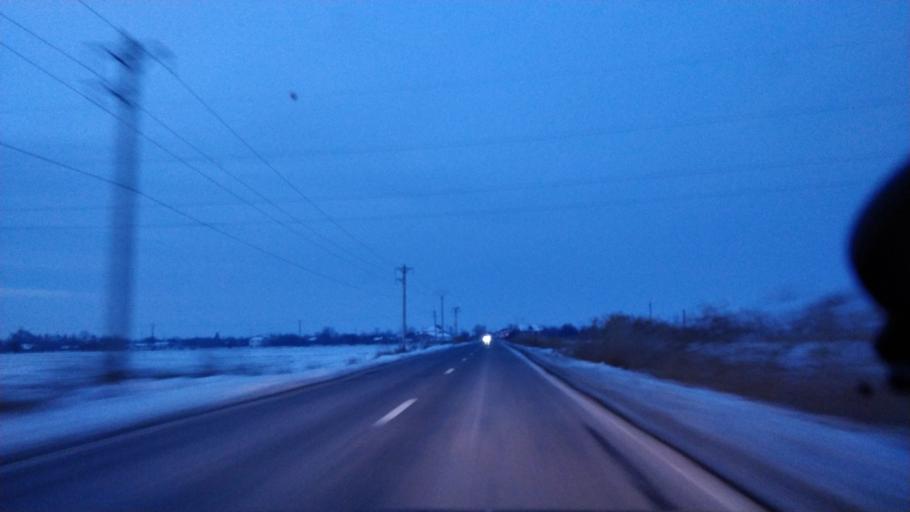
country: RO
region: Vrancea
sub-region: Comuna Nanesti
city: Nanesti
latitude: 45.5821
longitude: 27.4970
